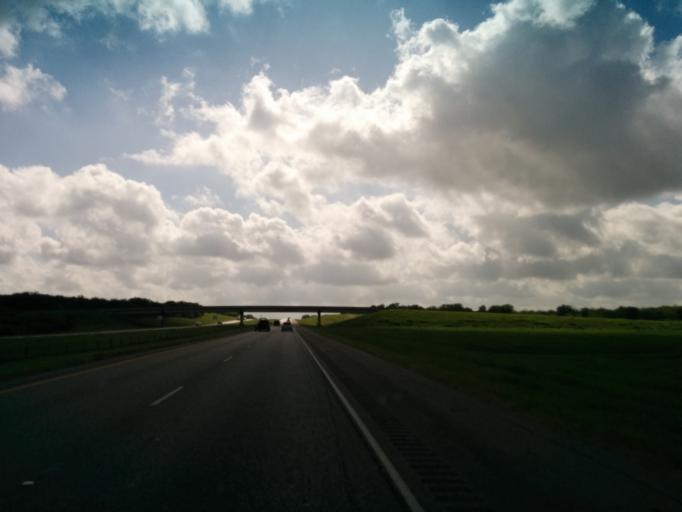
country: US
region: Texas
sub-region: Gonzales County
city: Waelder
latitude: 29.6639
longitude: -97.3656
